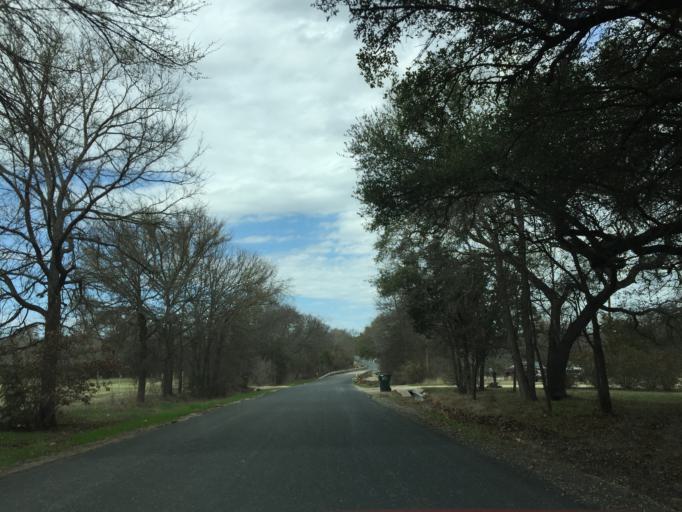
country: US
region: Texas
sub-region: Burnet County
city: Bertram
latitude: 30.7360
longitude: -97.9363
